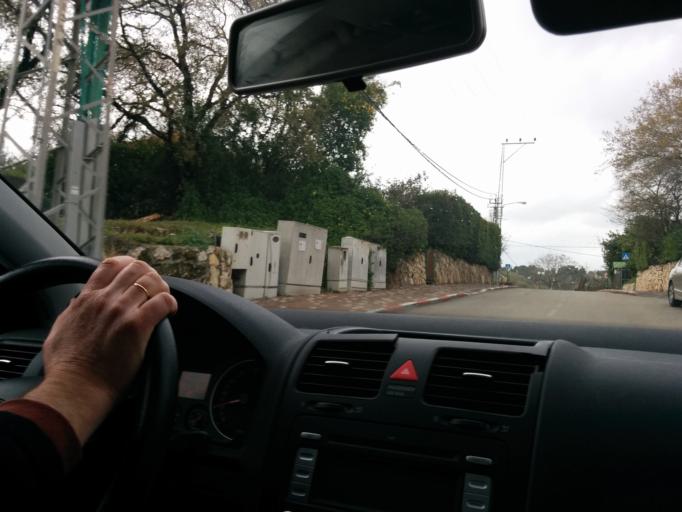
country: IL
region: Northern District
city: Basmat Tab`un
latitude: 32.7264
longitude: 35.1402
